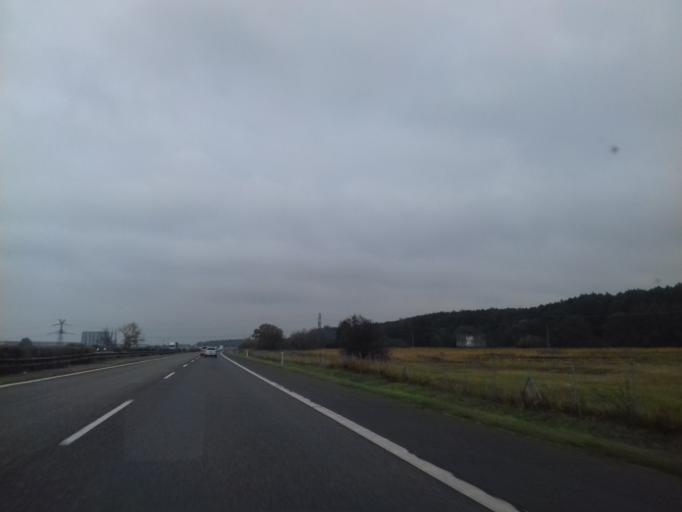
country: SK
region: Bratislavsky
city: Stupava
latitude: 48.3058
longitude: 17.0164
